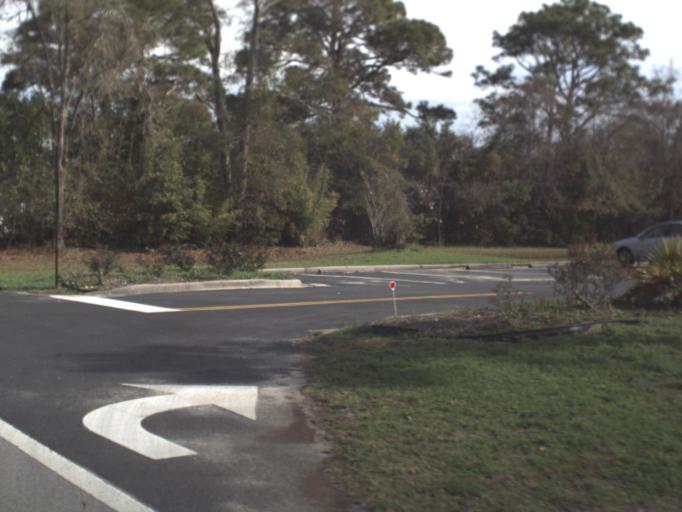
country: US
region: Florida
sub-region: Bay County
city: Pretty Bayou
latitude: 30.1977
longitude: -85.6833
